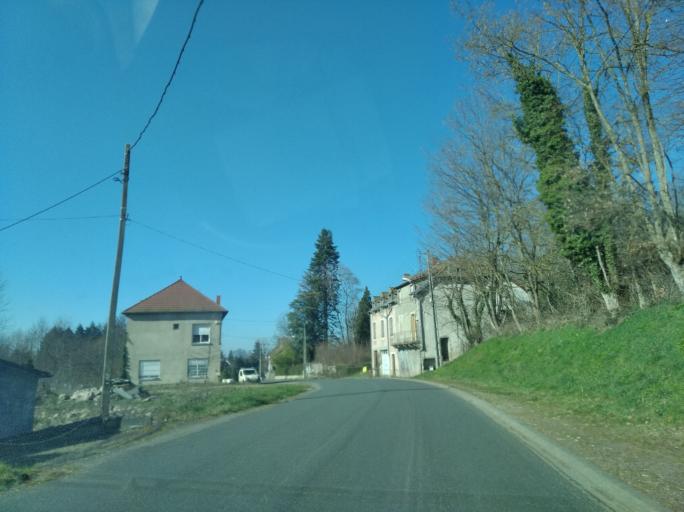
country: FR
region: Auvergne
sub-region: Departement de l'Allier
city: Le Mayet-de-Montagne
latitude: 46.0655
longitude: 3.6686
